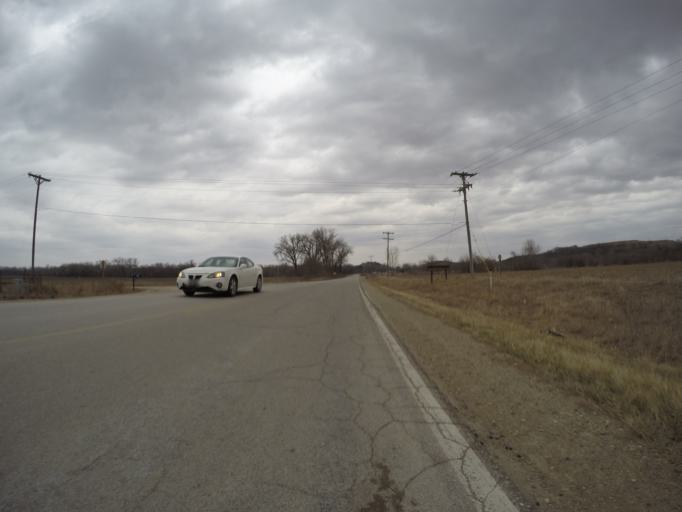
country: US
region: Kansas
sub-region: Riley County
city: Manhattan
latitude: 39.2401
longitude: -96.5715
